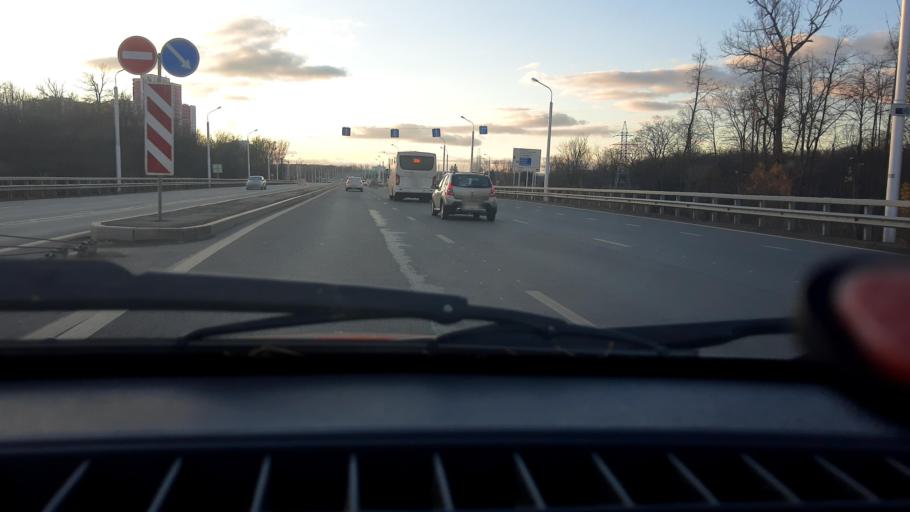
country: RU
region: Bashkortostan
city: Ufa
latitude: 54.7015
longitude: 55.8730
